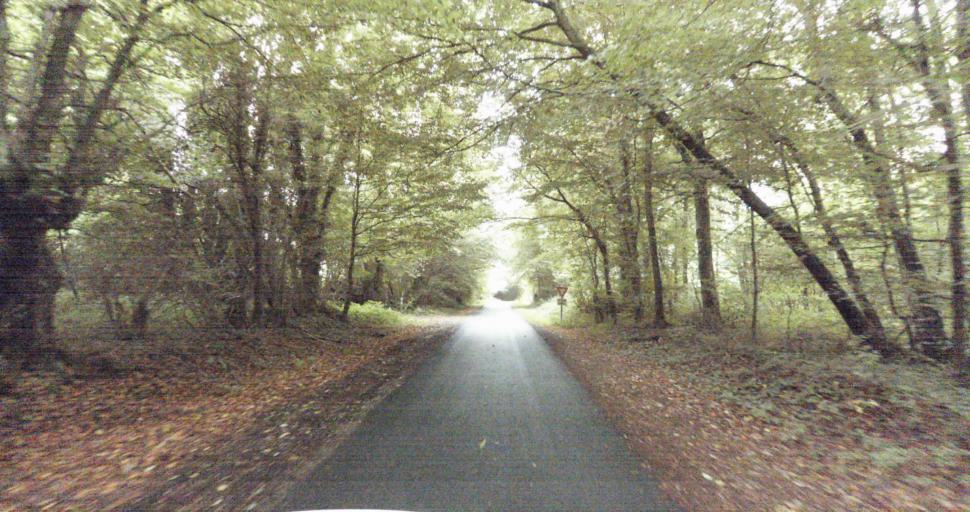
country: FR
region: Lower Normandy
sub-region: Departement de l'Orne
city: Vimoutiers
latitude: 48.8988
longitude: 0.1106
